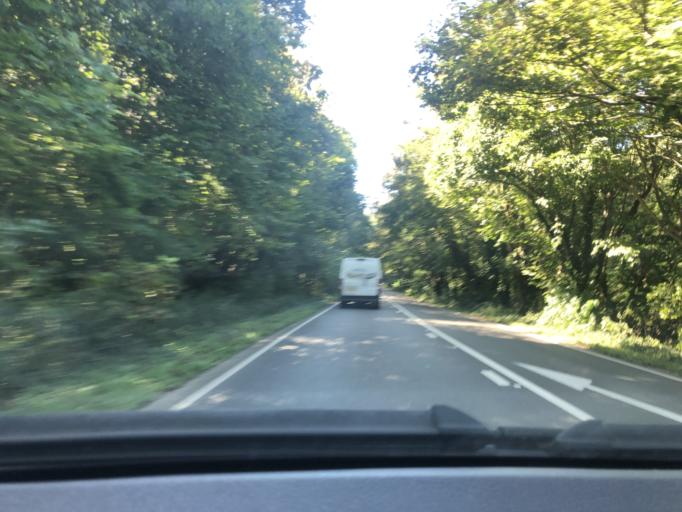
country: GB
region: England
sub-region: Somerset
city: Westonzoyland
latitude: 51.1314
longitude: -2.8417
